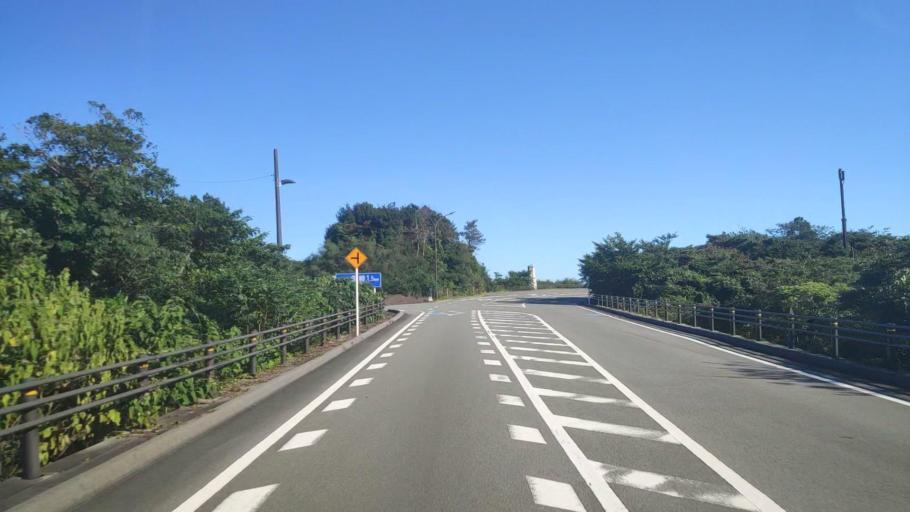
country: JP
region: Mie
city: Toba
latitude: 34.4188
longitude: 136.9141
